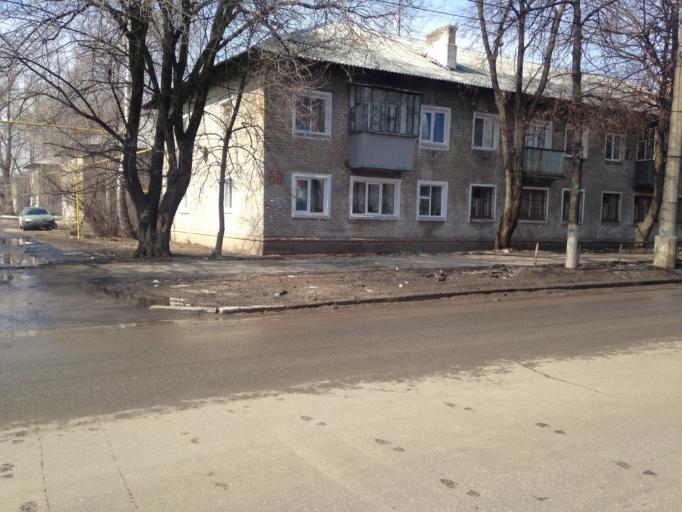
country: RU
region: Ulyanovsk
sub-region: Ulyanovskiy Rayon
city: Ulyanovsk
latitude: 54.3478
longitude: 48.5485
